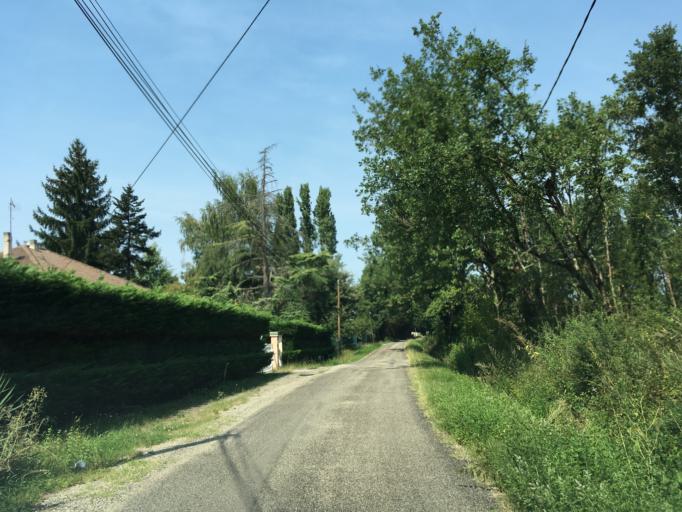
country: FR
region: Midi-Pyrenees
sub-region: Departement du Tarn-et-Garonne
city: Saint-Nauphary
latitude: 43.9750
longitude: 1.4020
